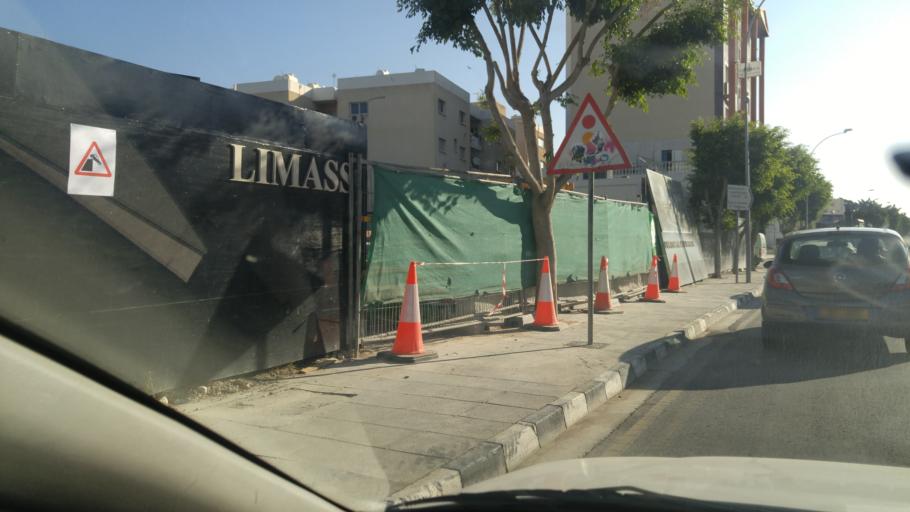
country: CY
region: Limassol
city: Limassol
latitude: 34.6878
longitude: 33.0434
